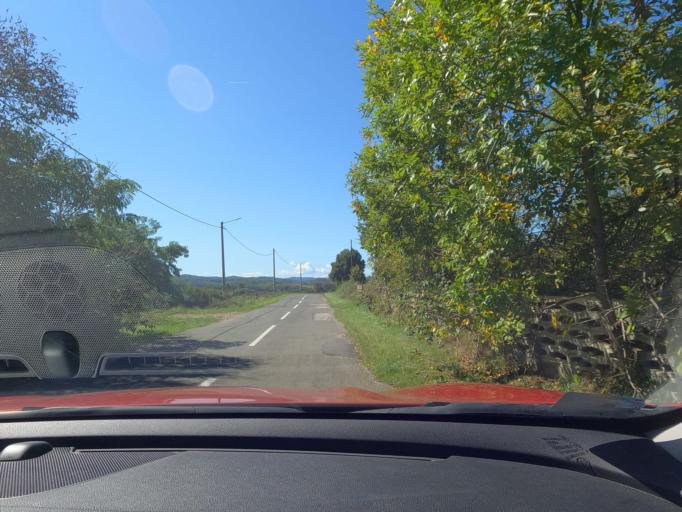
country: HR
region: Sisacko-Moslavacka
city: Petrinja
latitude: 45.3302
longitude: 16.2383
